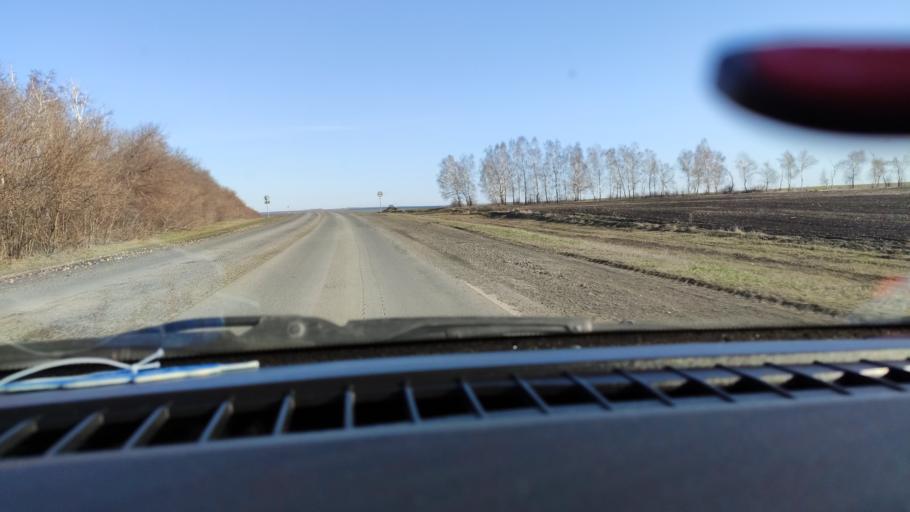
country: RU
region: Saratov
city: Dukhovnitskoye
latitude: 52.7187
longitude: 48.2653
